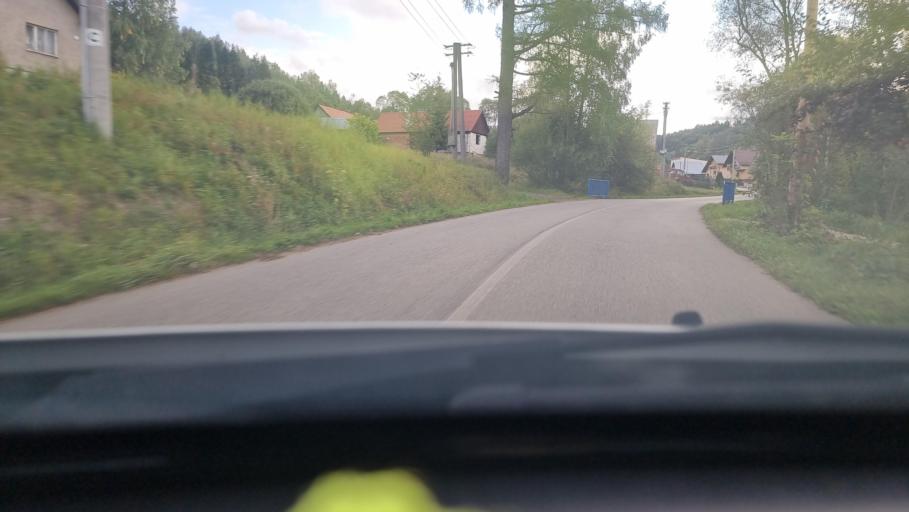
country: PL
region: Lesser Poland Voivodeship
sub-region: Powiat nowotarski
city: Szczawnica
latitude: 49.3585
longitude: 20.4470
